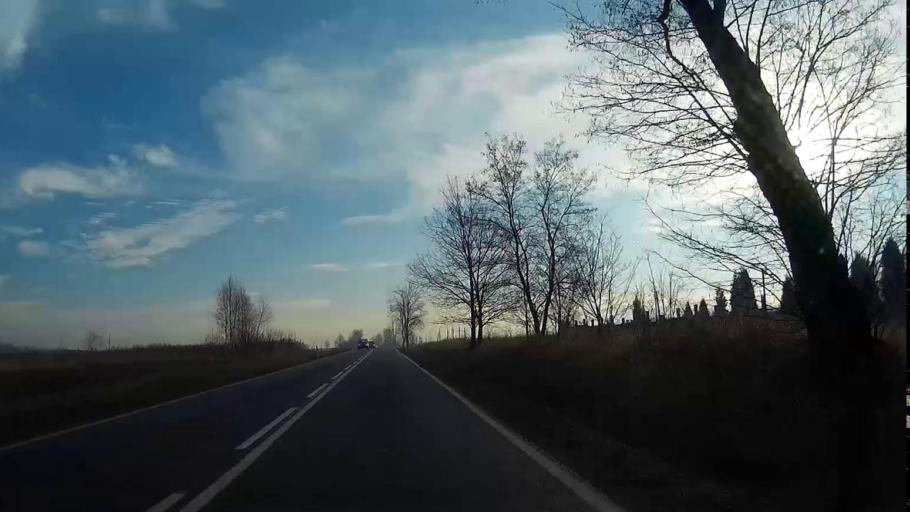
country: PL
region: Lesser Poland Voivodeship
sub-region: Powiat chrzanowski
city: Kwaczala
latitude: 50.0621
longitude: 19.5000
